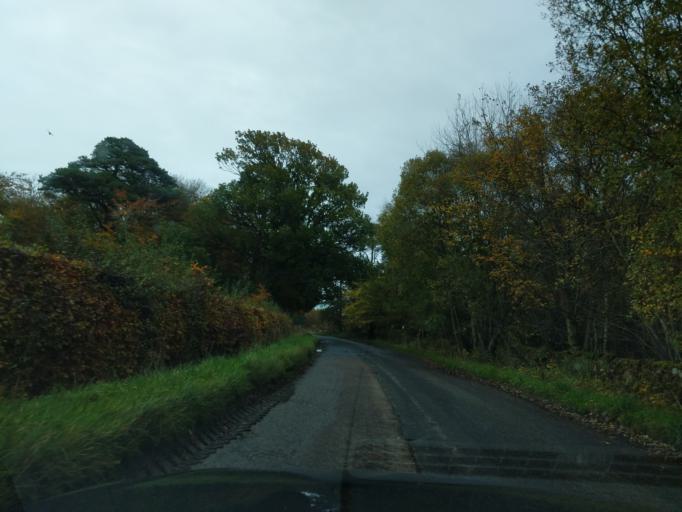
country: GB
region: Scotland
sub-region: Fife
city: Saint Andrews
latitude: 56.2876
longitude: -2.8225
